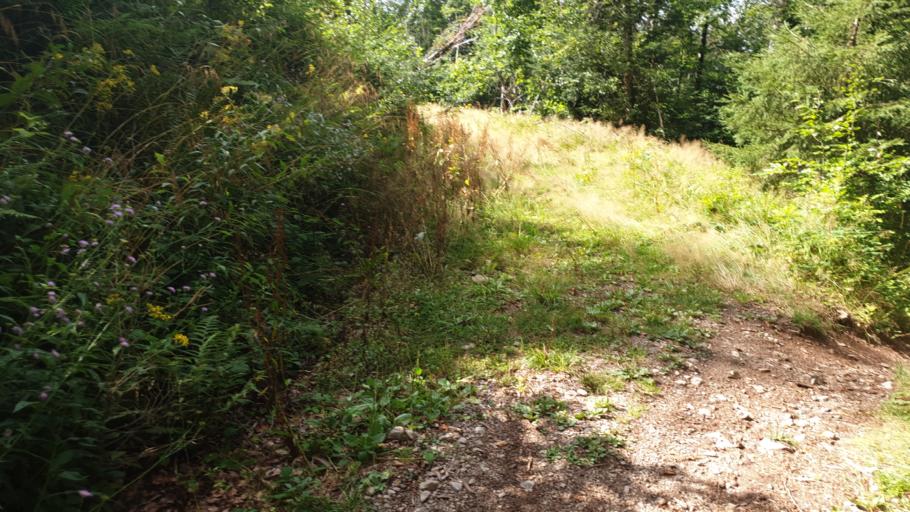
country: DE
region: Baden-Wuerttemberg
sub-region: Freiburg Region
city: Oberried
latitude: 47.9386
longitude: 7.9152
